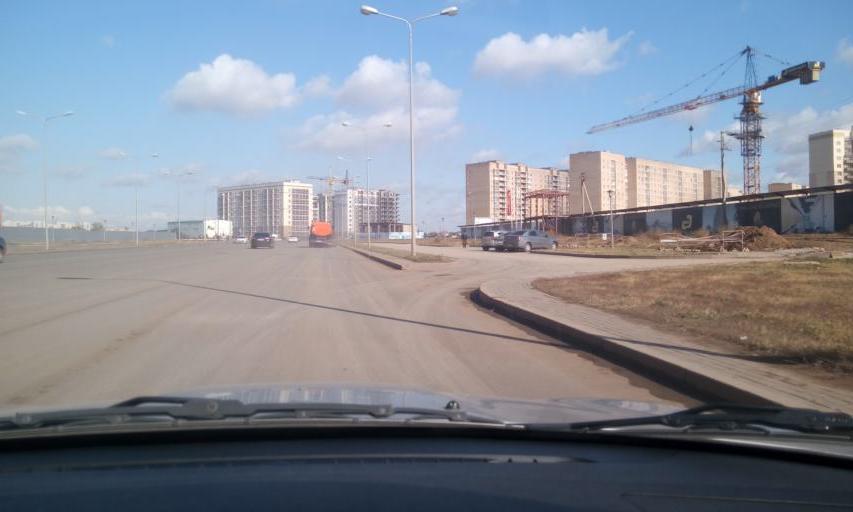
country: KZ
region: Astana Qalasy
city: Astana
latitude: 51.1230
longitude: 71.4865
